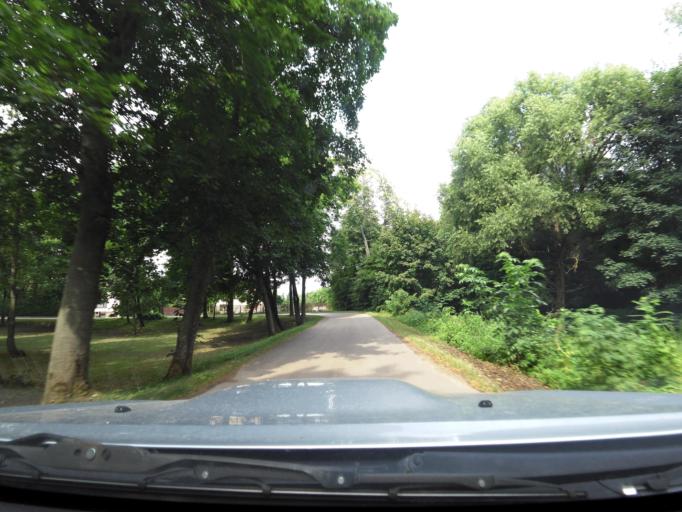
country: RU
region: Kaliningrad
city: Sovetsk
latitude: 55.0870
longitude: 21.9085
